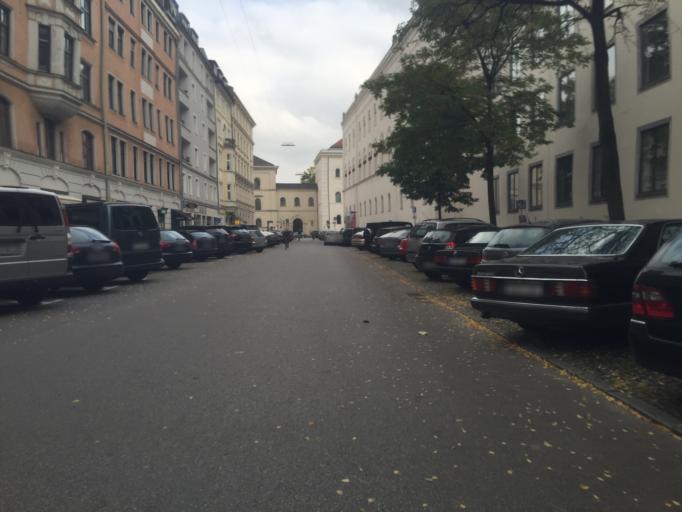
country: DE
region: Bavaria
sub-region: Upper Bavaria
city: Munich
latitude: 48.1518
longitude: 11.5799
